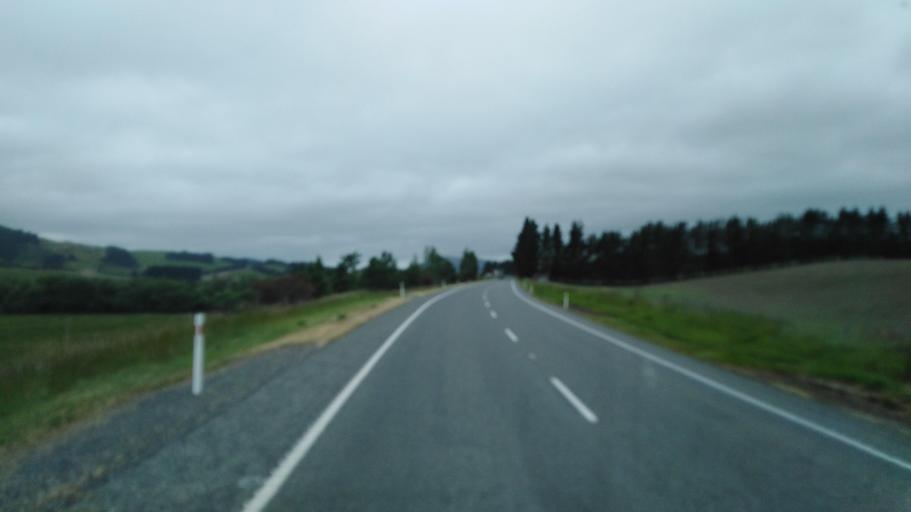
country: NZ
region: Canterbury
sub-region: Hurunui District
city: Amberley
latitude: -42.9570
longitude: 172.9989
